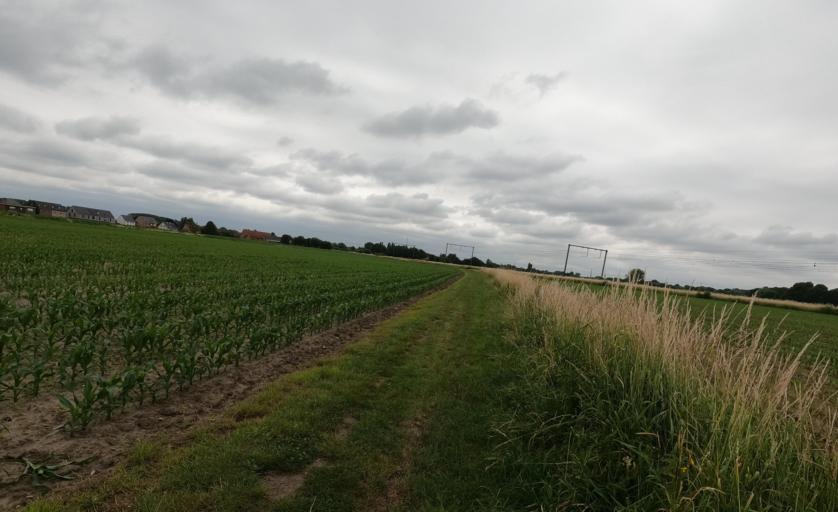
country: BE
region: Flanders
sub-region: Provincie Antwerpen
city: Berlaar
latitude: 51.1079
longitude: 4.6502
